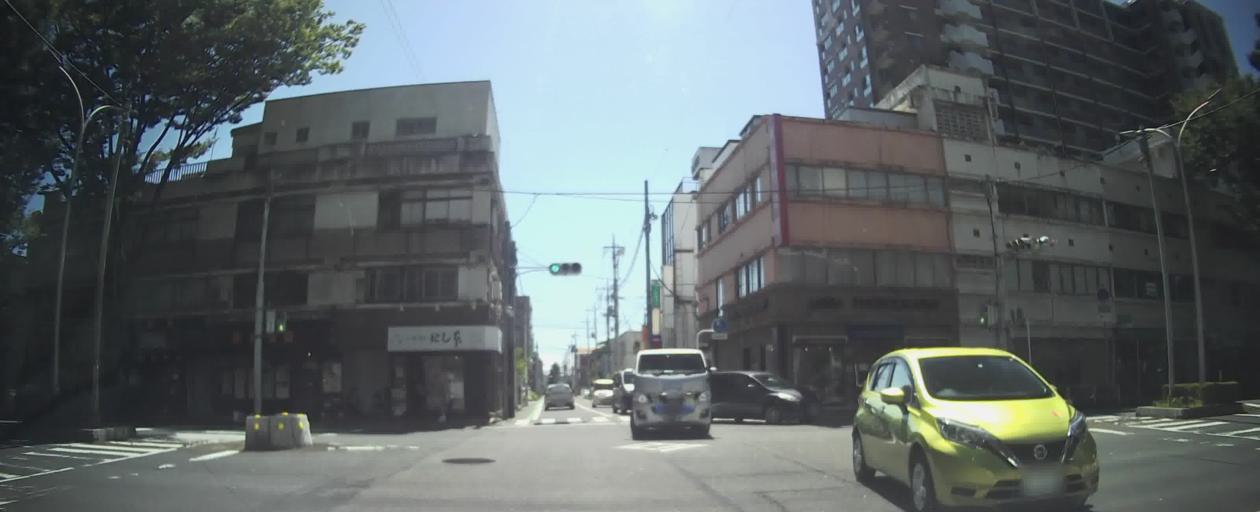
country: JP
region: Gunma
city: Maebashi-shi
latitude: 36.3911
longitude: 139.0653
